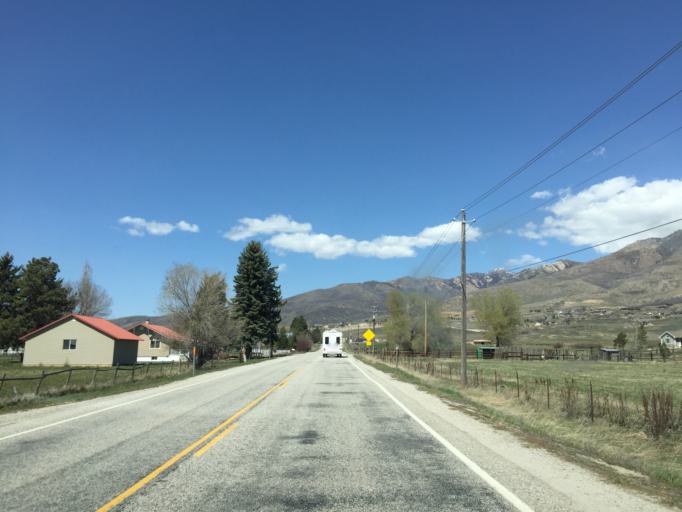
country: US
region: Utah
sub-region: Weber County
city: Wolf Creek
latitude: 41.3068
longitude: -111.8253
